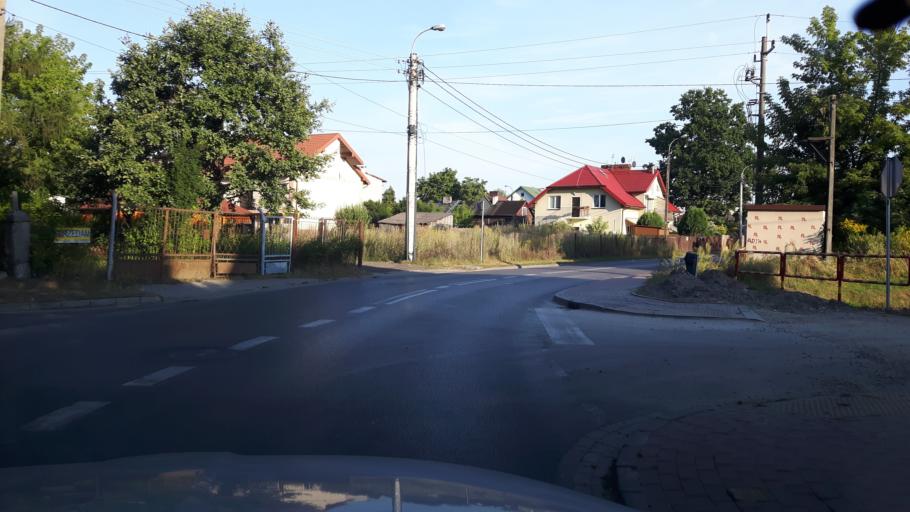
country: PL
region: Masovian Voivodeship
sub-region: Powiat wolominski
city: Kobylka
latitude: 52.3477
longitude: 21.2085
